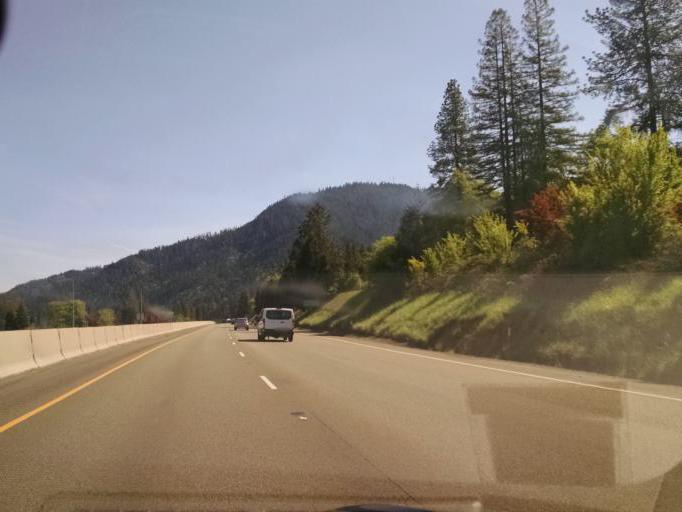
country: US
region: Oregon
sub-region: Douglas County
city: Canyonville
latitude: 42.9369
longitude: -123.2851
